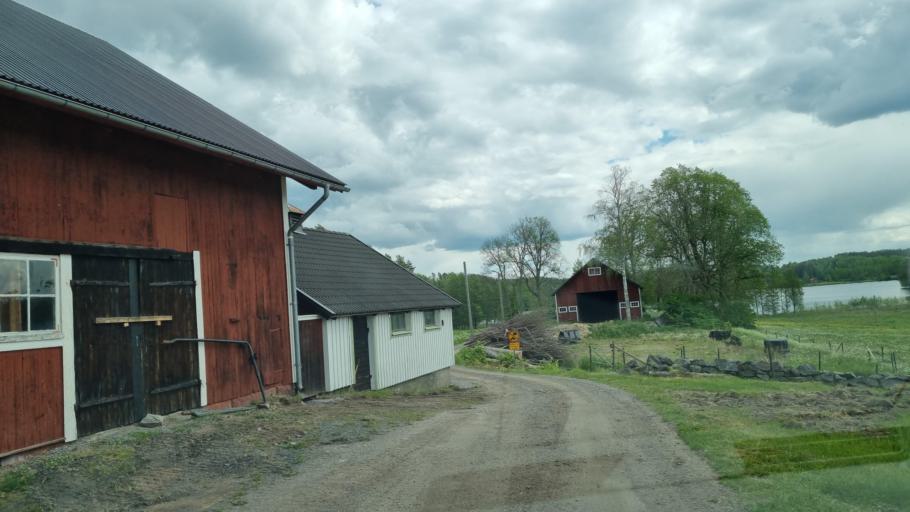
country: SE
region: OEstergoetland
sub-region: Atvidabergs Kommun
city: Atvidaberg
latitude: 58.1908
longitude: 16.0437
